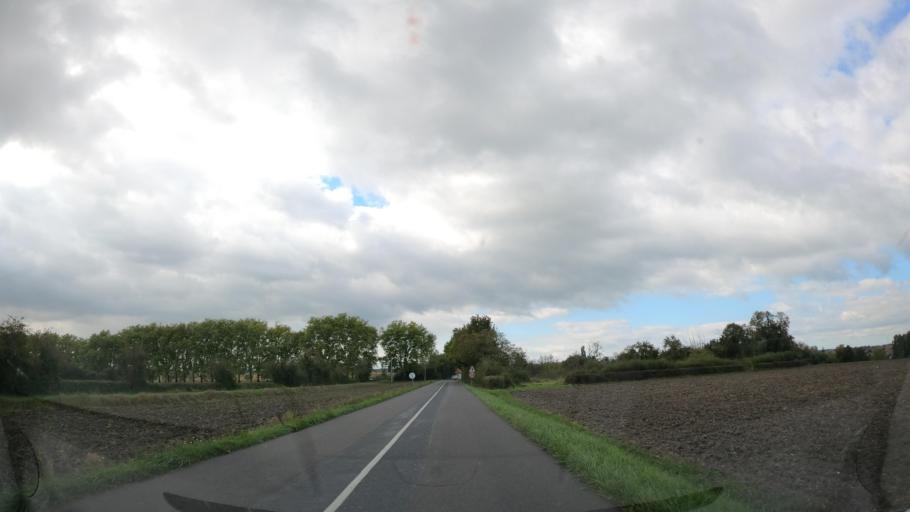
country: FR
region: Auvergne
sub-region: Departement de l'Allier
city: Lapalisse
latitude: 46.3700
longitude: 3.6134
